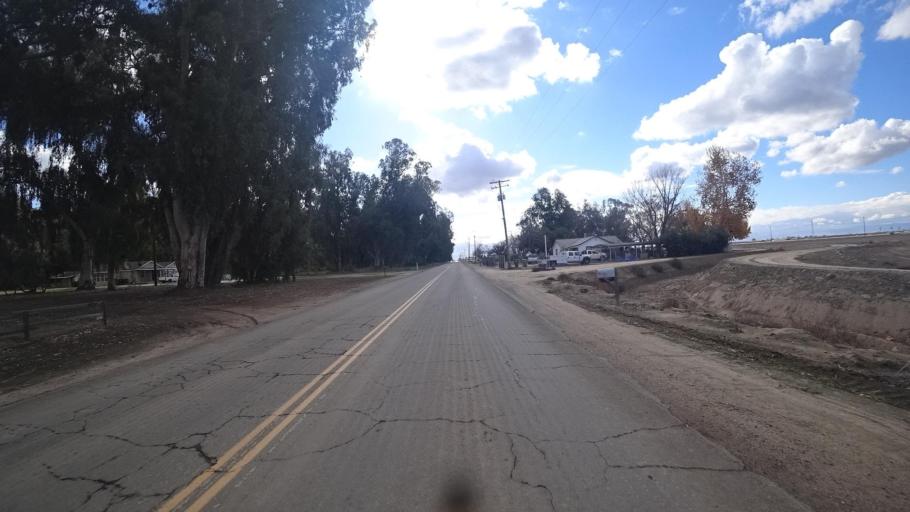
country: US
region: California
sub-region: Kern County
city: Greenfield
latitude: 35.2361
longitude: -119.0918
